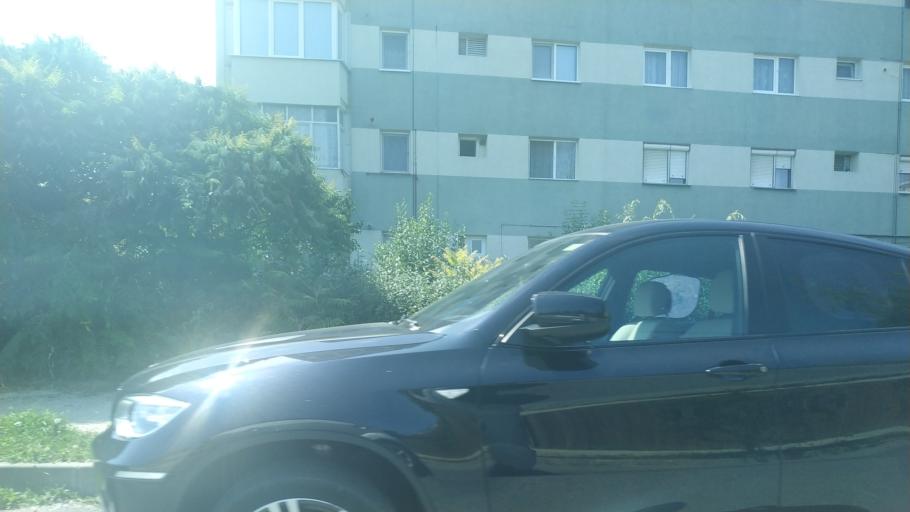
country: RO
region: Brasov
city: Fogarasch
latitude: 45.8395
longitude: 24.9703
